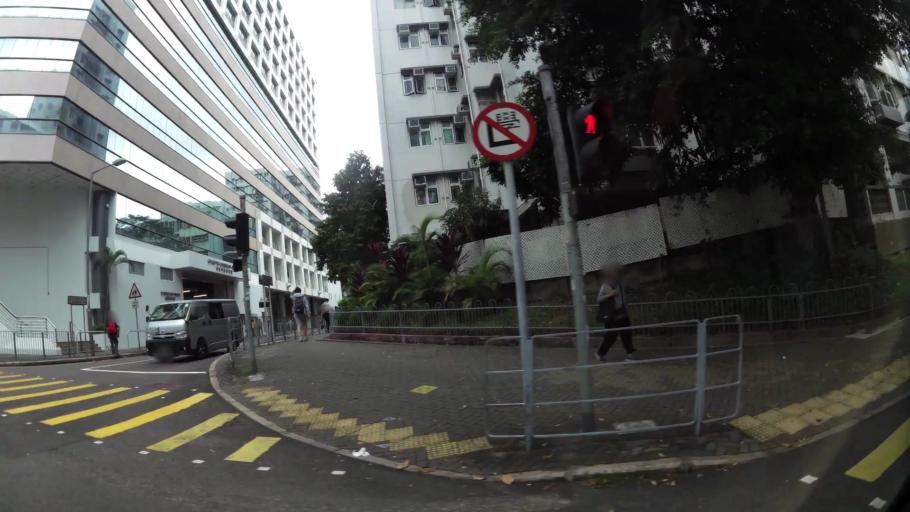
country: HK
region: Kowloon City
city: Kowloon
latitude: 22.3152
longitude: 114.1800
